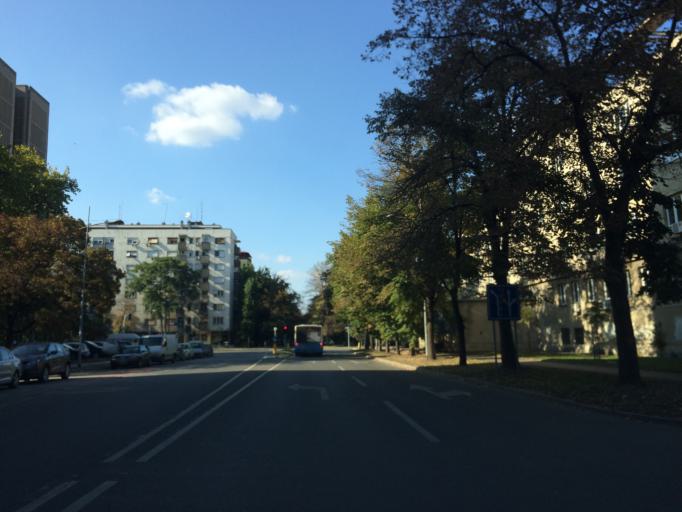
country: RS
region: Autonomna Pokrajina Vojvodina
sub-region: Juznobacki Okrug
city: Novi Sad
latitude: 45.2602
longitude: 19.8345
